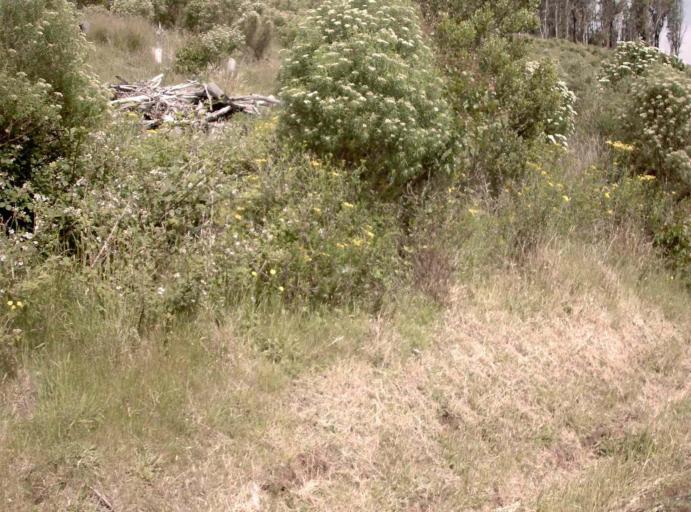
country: AU
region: Victoria
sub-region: Latrobe
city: Traralgon
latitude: -38.3555
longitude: 146.5694
